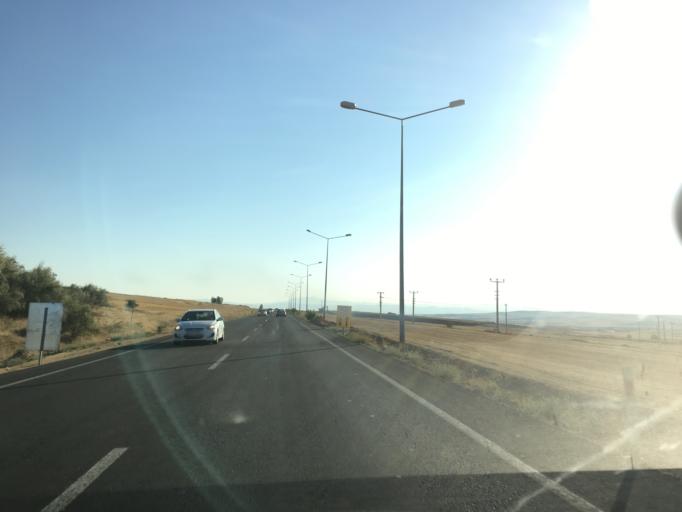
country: TR
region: Nevsehir
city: Hacibektas
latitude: 38.9301
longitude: 34.5539
